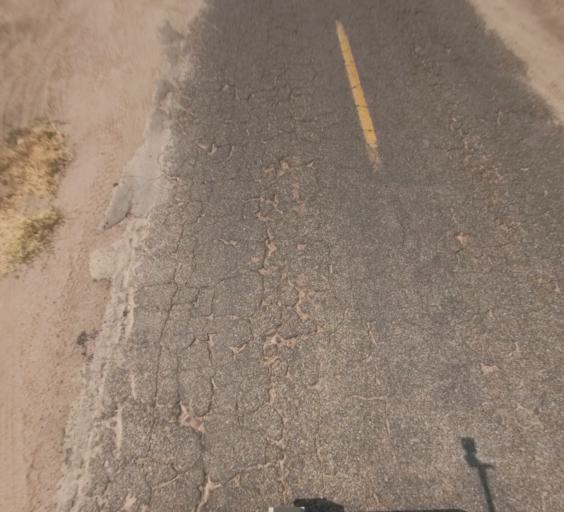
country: US
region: California
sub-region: Madera County
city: Fairmead
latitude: 37.0947
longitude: -120.1930
